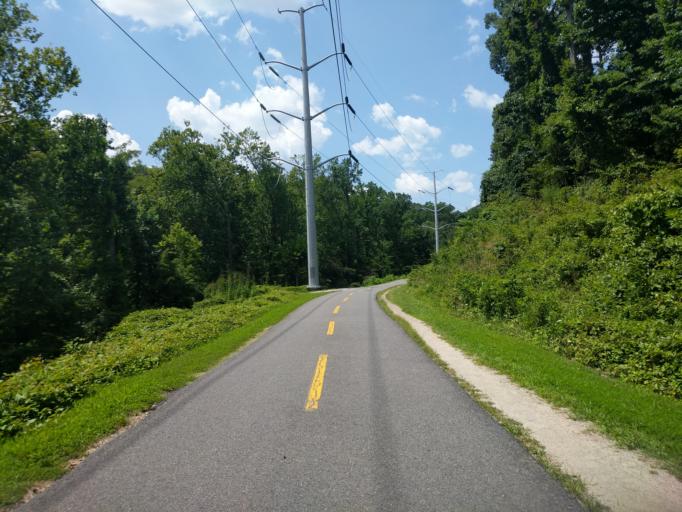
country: US
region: Virginia
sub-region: Fairfax County
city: Baileys Crossroads
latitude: 38.8623
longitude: -77.1165
